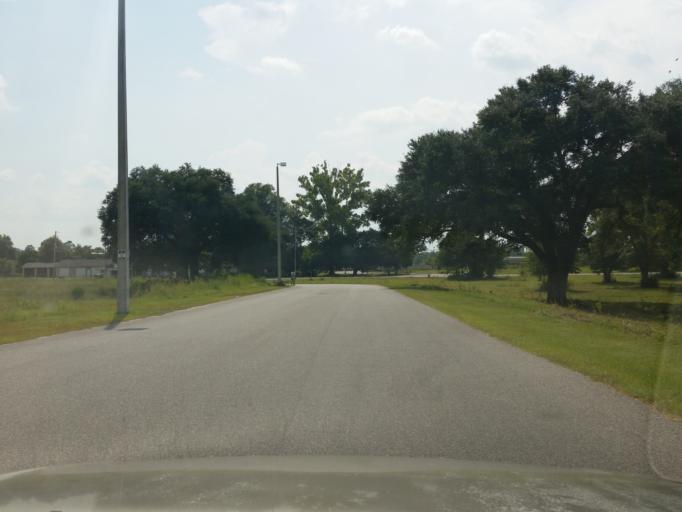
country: US
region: Florida
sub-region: Escambia County
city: Ensley
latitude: 30.5319
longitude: -87.2821
